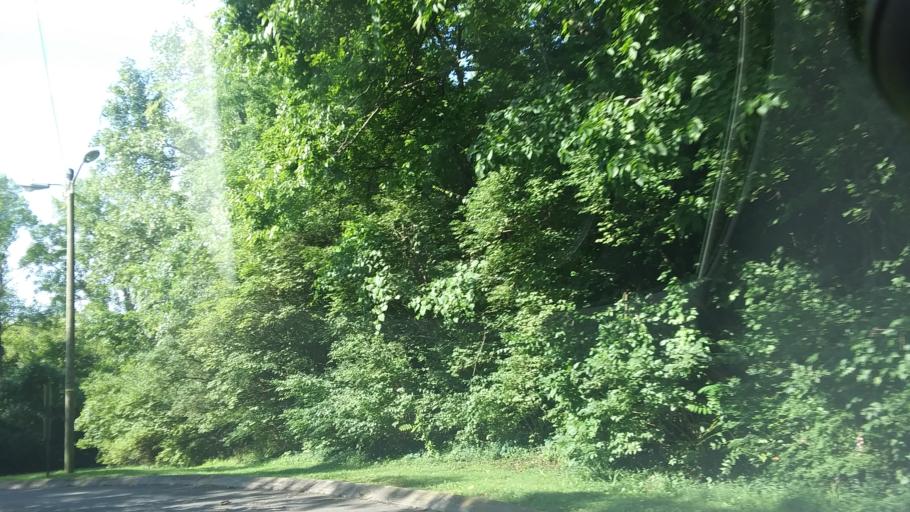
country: US
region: Tennessee
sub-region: Davidson County
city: Belle Meade
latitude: 36.0772
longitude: -86.8896
